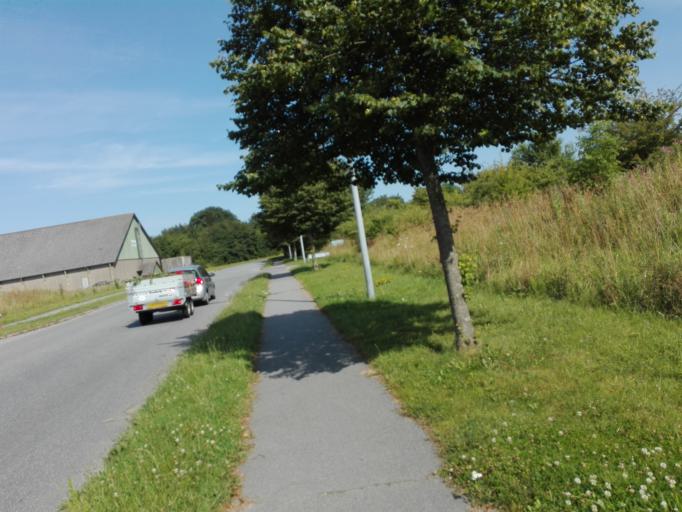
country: DK
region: Central Jutland
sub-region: Arhus Kommune
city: Tranbjerg
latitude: 56.1033
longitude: 10.1138
